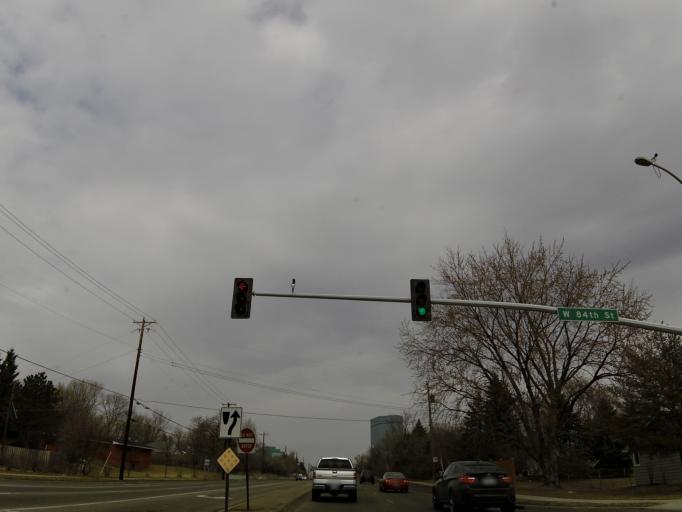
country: US
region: Minnesota
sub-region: Hennepin County
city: Bloomington
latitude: 44.8517
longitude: -93.3291
